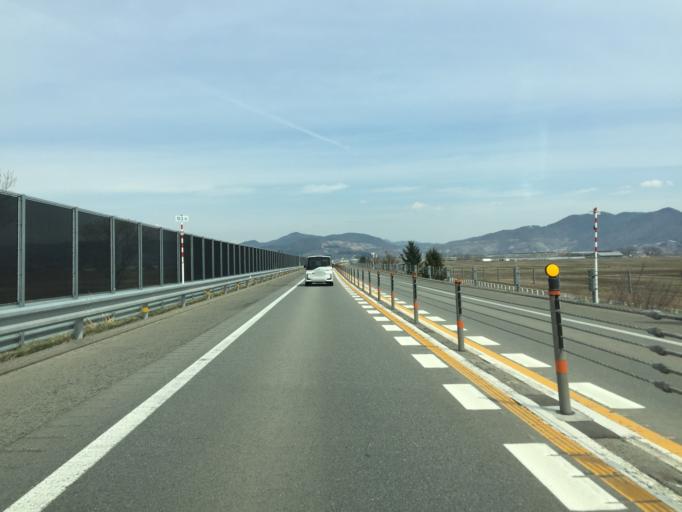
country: JP
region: Yamagata
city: Takahata
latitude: 38.0138
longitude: 140.1576
